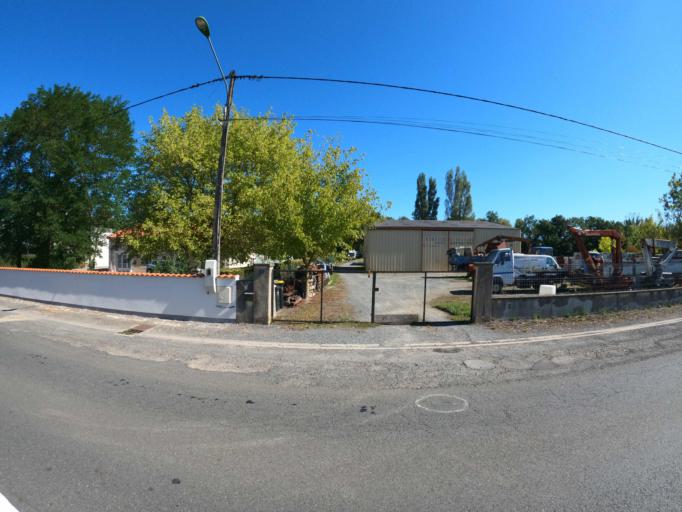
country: FR
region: Poitou-Charentes
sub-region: Departement de la Vienne
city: Lathus-Saint-Remy
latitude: 46.3436
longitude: 0.9520
